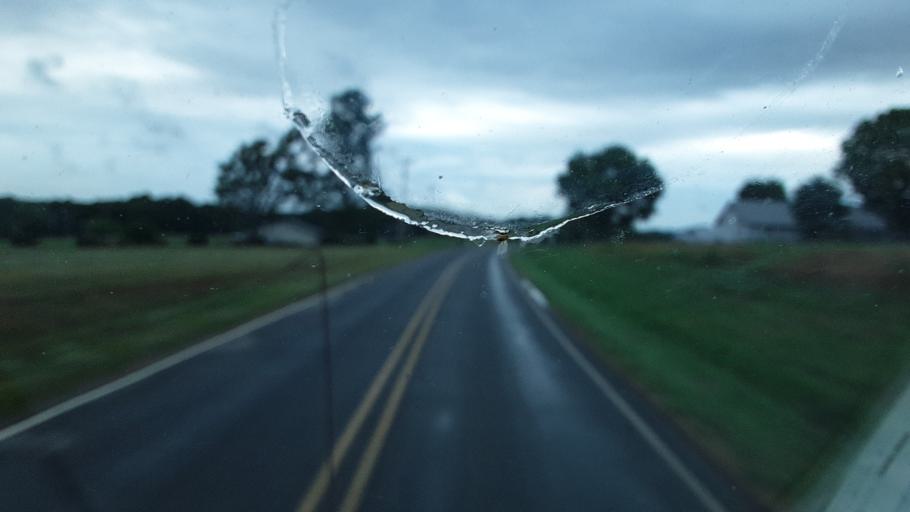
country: US
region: North Carolina
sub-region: Yadkin County
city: Jonesville
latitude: 36.0983
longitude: -80.8629
